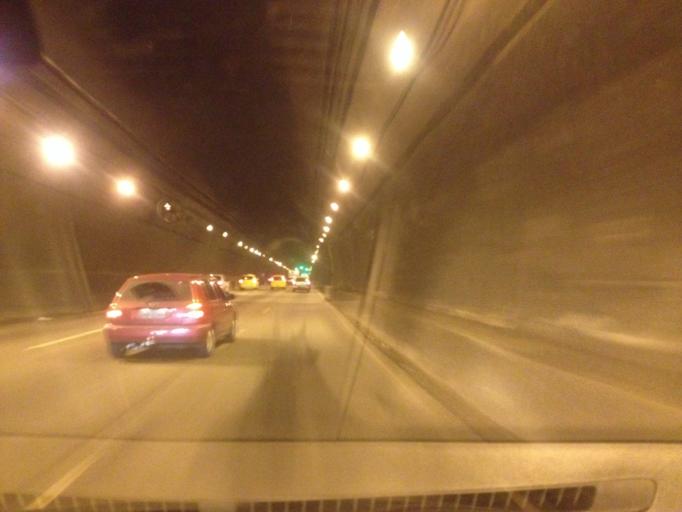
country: BR
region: Rio de Janeiro
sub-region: Rio De Janeiro
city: Rio de Janeiro
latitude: -22.9579
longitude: -43.2044
